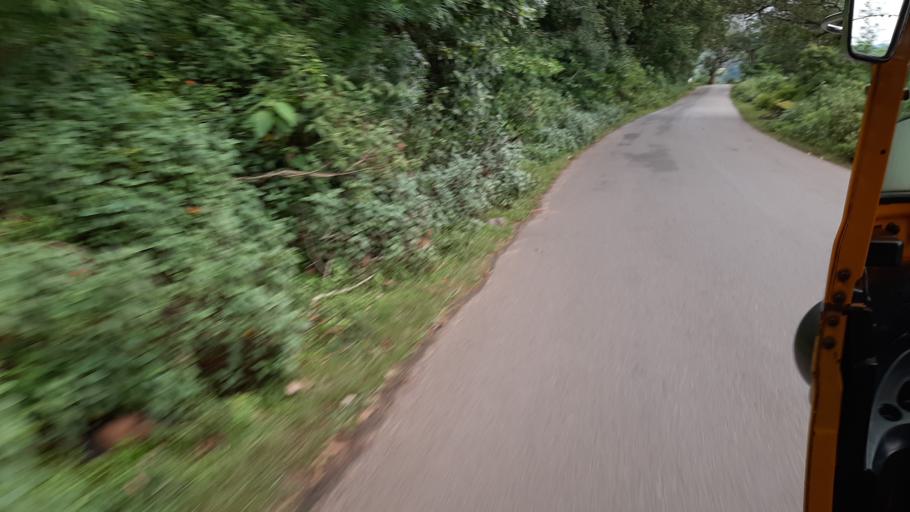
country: IN
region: Andhra Pradesh
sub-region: Vizianagaram District
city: Salur
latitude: 18.2460
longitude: 83.0237
